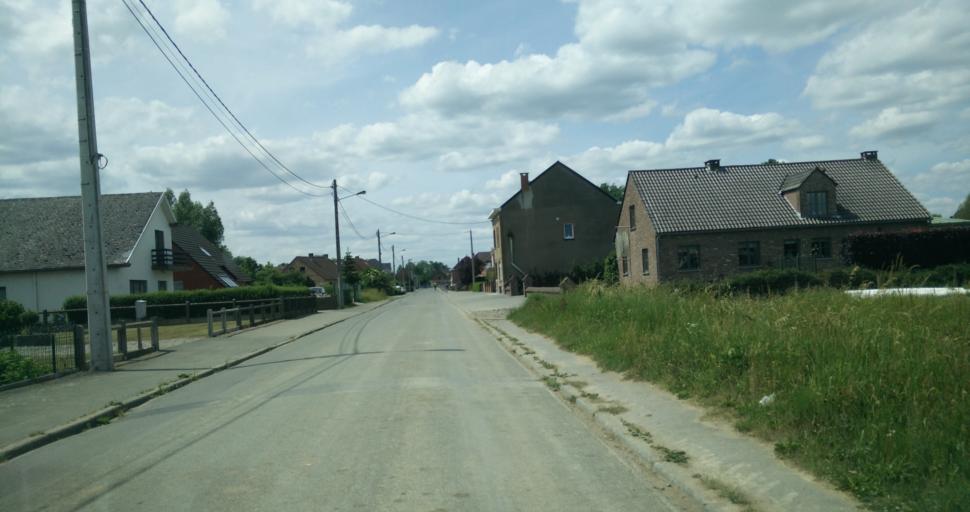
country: BE
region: Wallonia
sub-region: Province du Hainaut
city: Lessines
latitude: 50.7273
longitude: 3.8617
